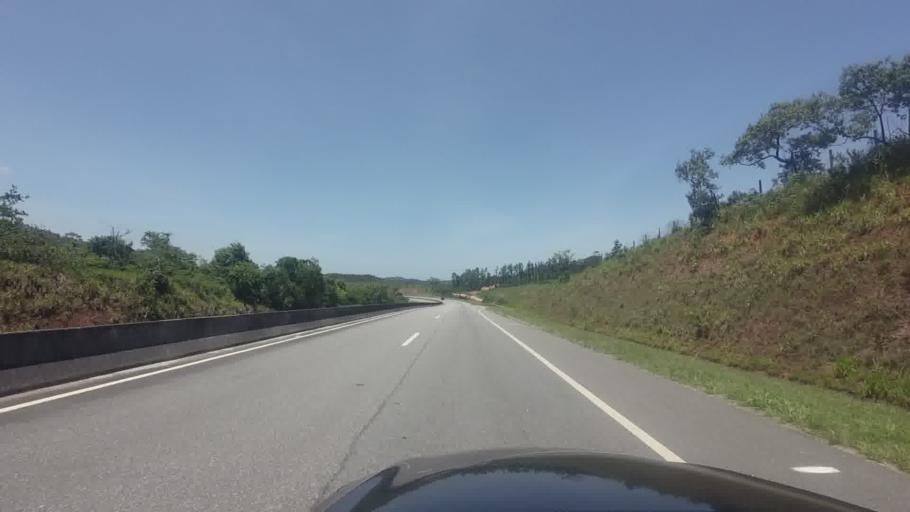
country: BR
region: Espirito Santo
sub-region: Guarapari
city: Guarapari
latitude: -20.6253
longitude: -40.4983
